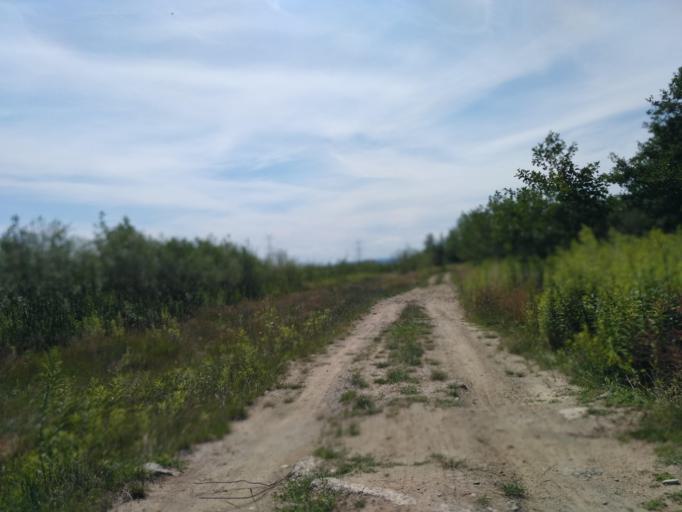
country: PL
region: Subcarpathian Voivodeship
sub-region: Powiat krosnienski
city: Kroscienko Wyzne
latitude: 49.6457
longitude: 21.8514
